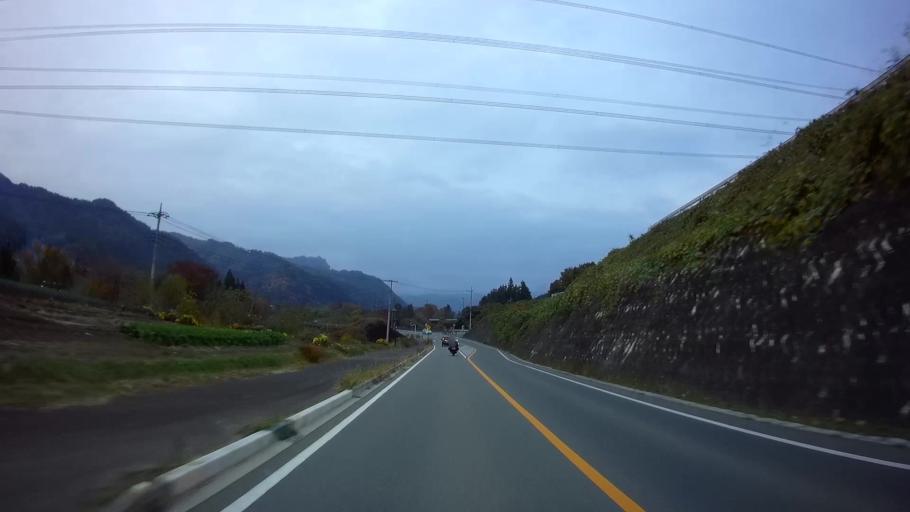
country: JP
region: Gunma
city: Nakanojomachi
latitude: 36.5607
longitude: 138.7547
